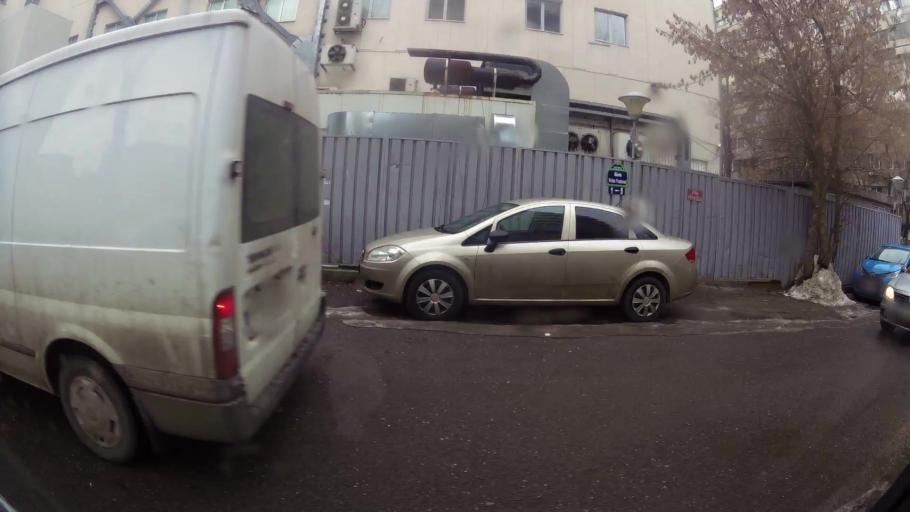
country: RO
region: Ilfov
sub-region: Comuna Chiajna
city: Rosu
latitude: 44.4212
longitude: 26.0382
